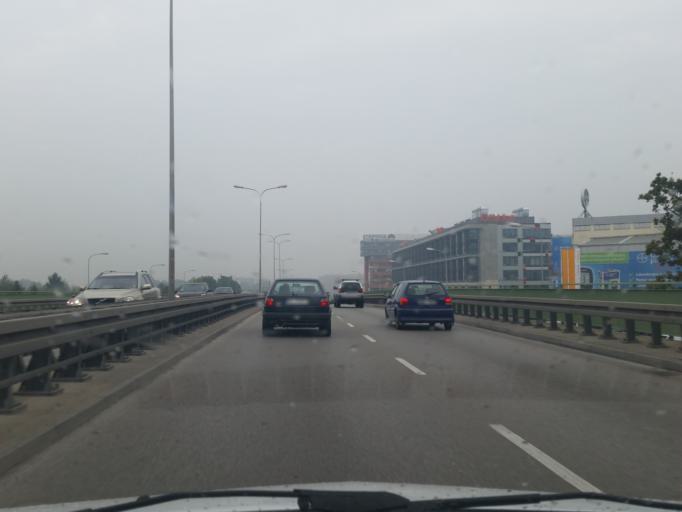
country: PL
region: Masovian Voivodeship
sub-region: Warszawa
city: Wlochy
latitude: 52.2100
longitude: 20.9492
